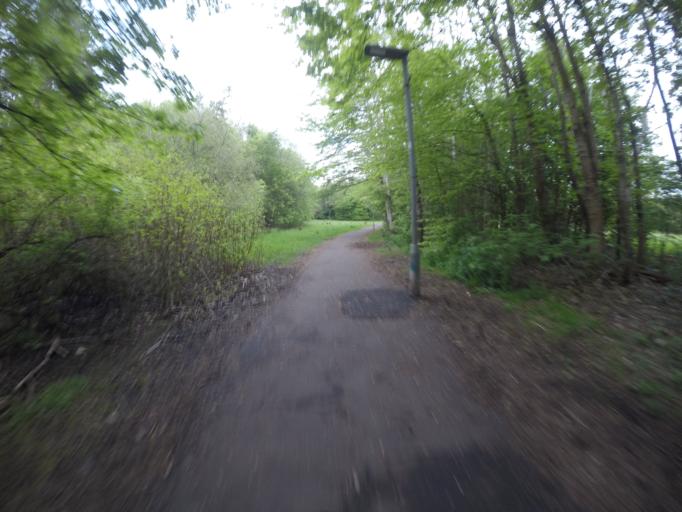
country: GB
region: Scotland
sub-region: North Ayrshire
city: Irvine
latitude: 55.6333
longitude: -4.6409
